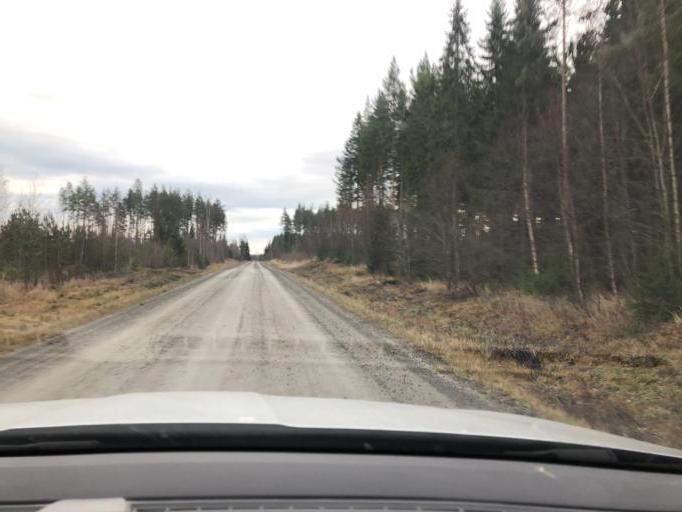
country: SE
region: Gaevleborg
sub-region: Hudiksvalls Kommun
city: Sorforsa
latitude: 61.6483
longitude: 16.9338
